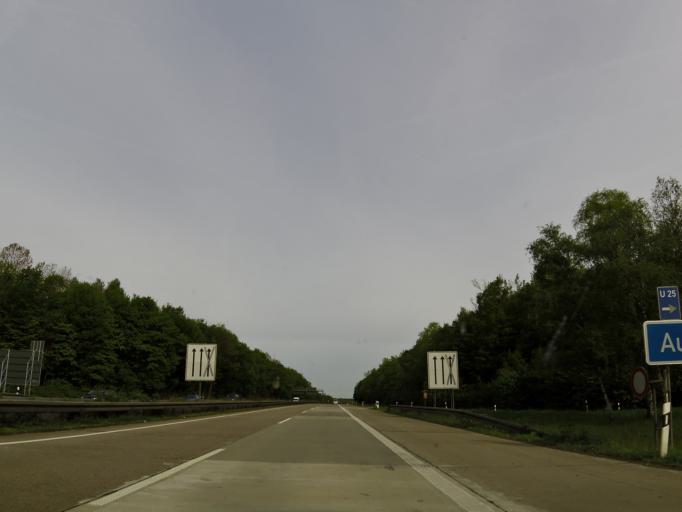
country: DE
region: Lower Saxony
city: Holle
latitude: 52.1038
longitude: 10.1449
